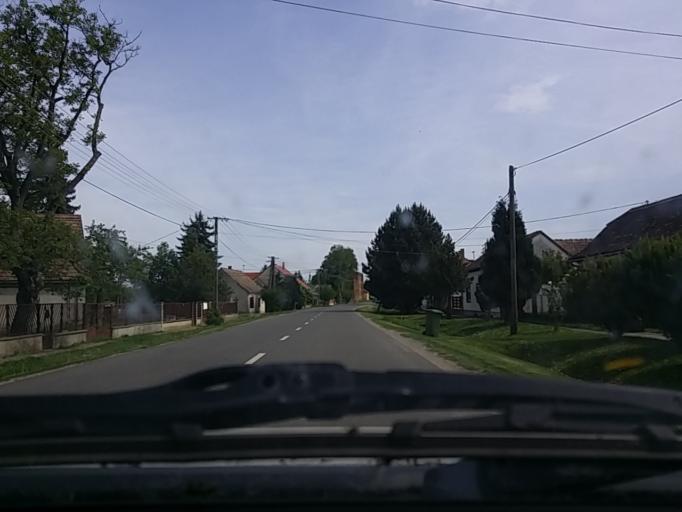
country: HR
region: Osjecko-Baranjska
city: Viljevo
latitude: 45.8281
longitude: 18.0966
